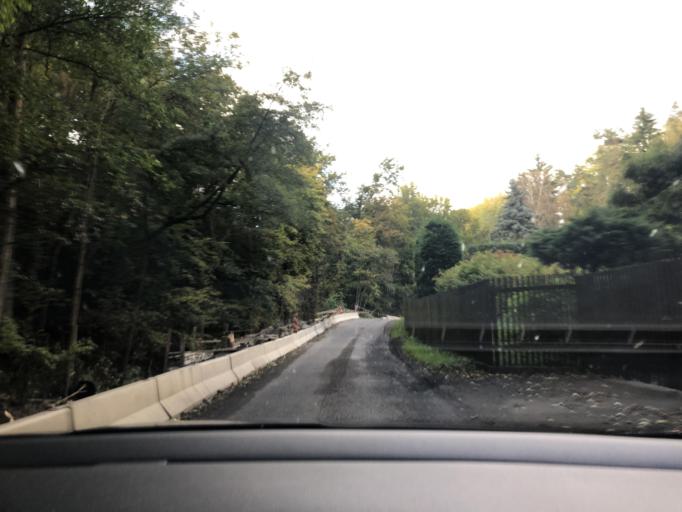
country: CZ
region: Ustecky
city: Velke Brezno
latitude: 50.6347
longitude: 14.1572
